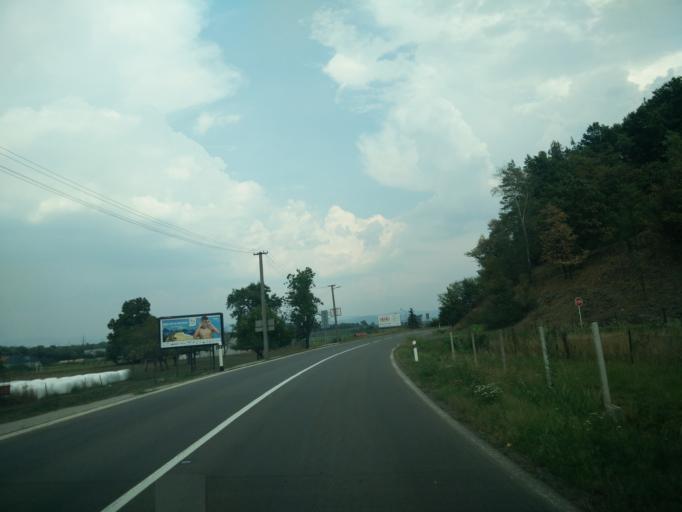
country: SK
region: Banskobystricky
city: Zarnovica
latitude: 48.5297
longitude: 18.7429
